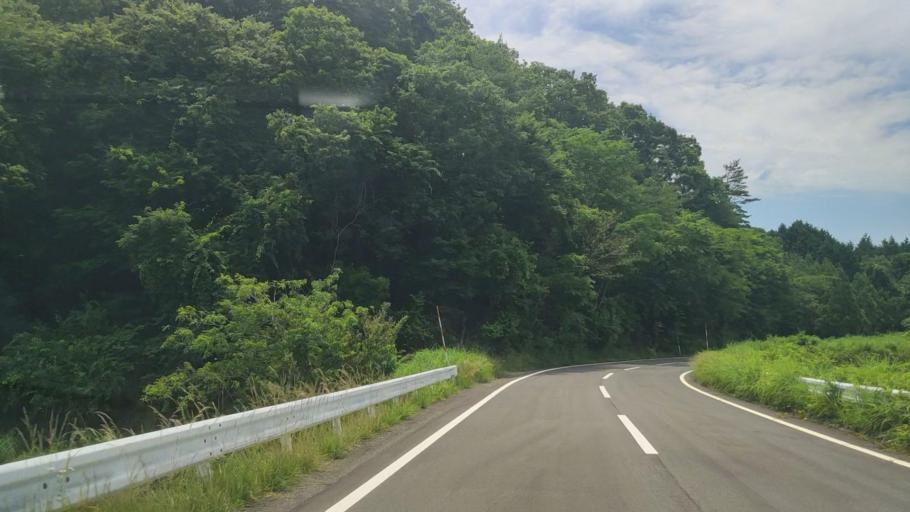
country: JP
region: Hyogo
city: Toyooka
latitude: 35.5109
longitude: 134.6854
